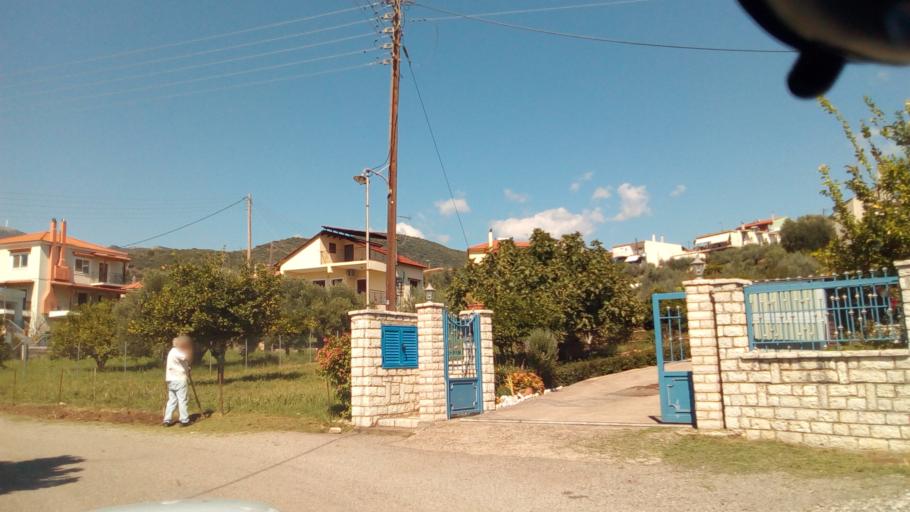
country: GR
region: West Greece
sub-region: Nomos Aitolias kai Akarnanias
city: Nafpaktos
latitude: 38.4147
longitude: 21.8964
